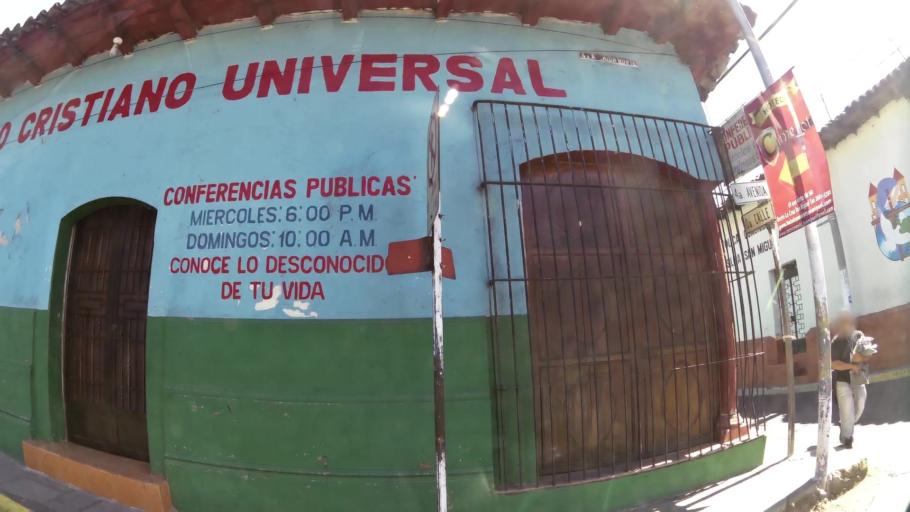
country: SV
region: San Miguel
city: San Miguel
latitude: 13.4860
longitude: -88.1753
